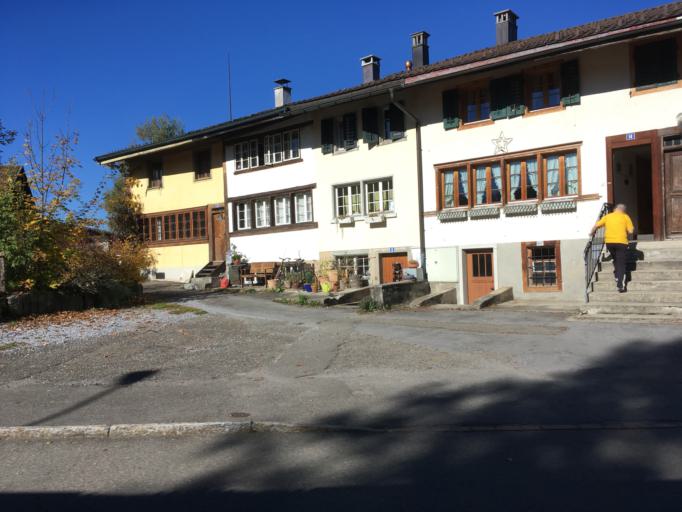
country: CH
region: Zurich
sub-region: Bezirk Hinwil
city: Baretswil
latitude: 47.3338
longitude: 8.8572
